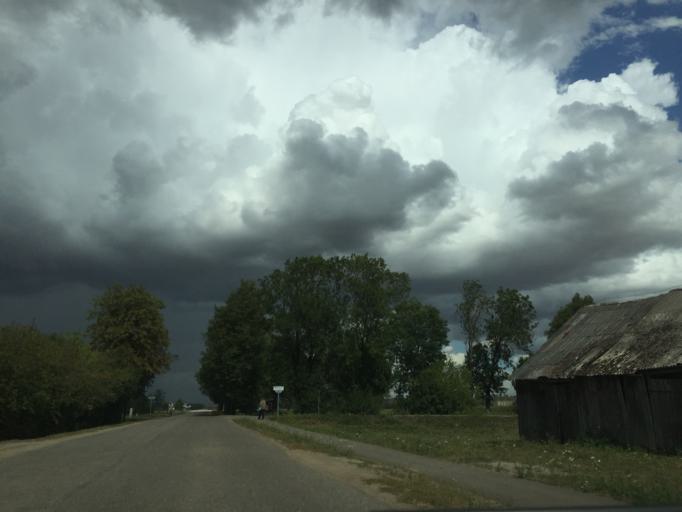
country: LT
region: Siauliu apskritis
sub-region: Joniskis
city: Joniskis
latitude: 56.2739
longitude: 23.7441
